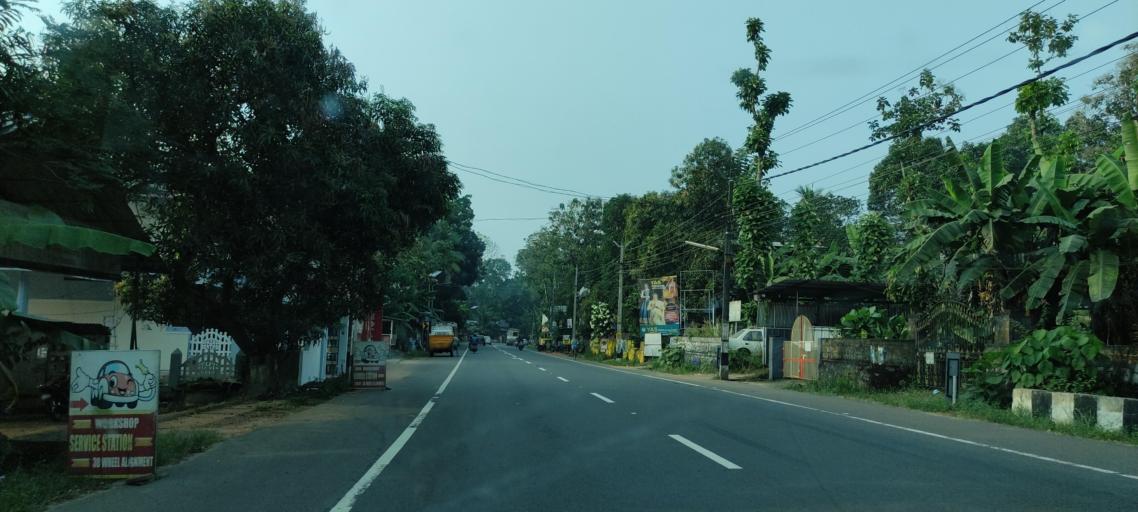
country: IN
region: Kerala
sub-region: Pattanamtitta
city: Adur
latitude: 9.0998
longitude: 76.7513
